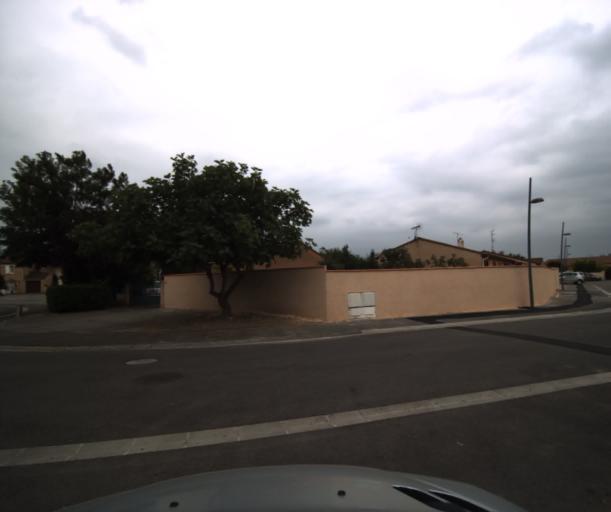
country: FR
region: Midi-Pyrenees
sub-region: Departement de la Haute-Garonne
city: Portet-sur-Garonne
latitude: 43.5439
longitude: 1.4141
